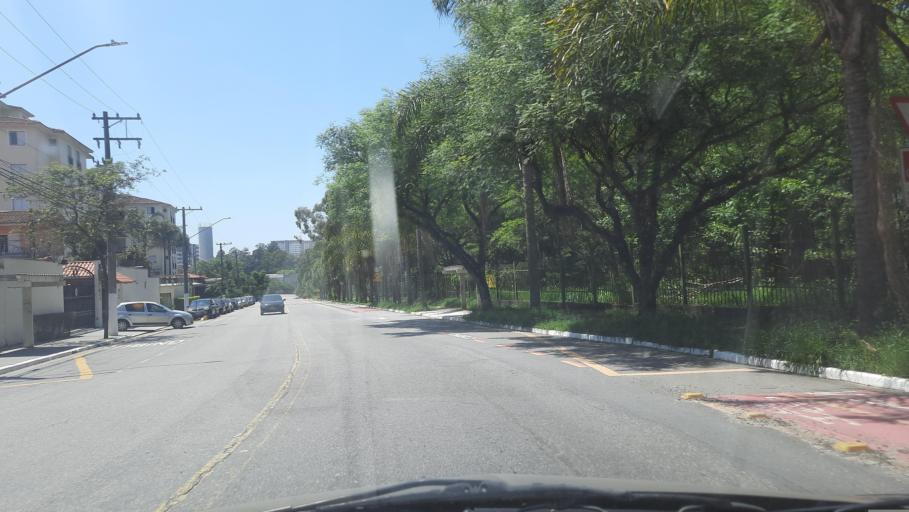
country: BR
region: Sao Paulo
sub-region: Caieiras
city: Caieiras
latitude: -23.4428
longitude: -46.7300
